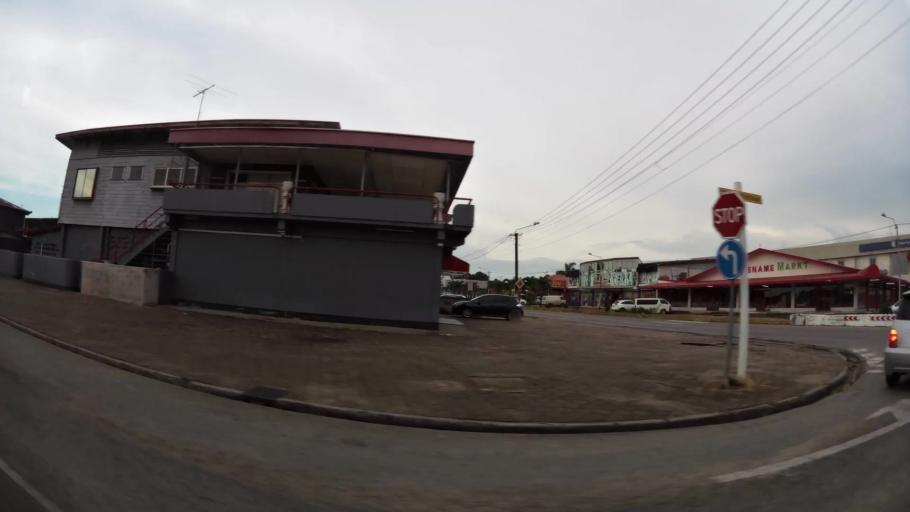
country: SR
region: Paramaribo
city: Paramaribo
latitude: 5.8151
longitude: -55.1882
